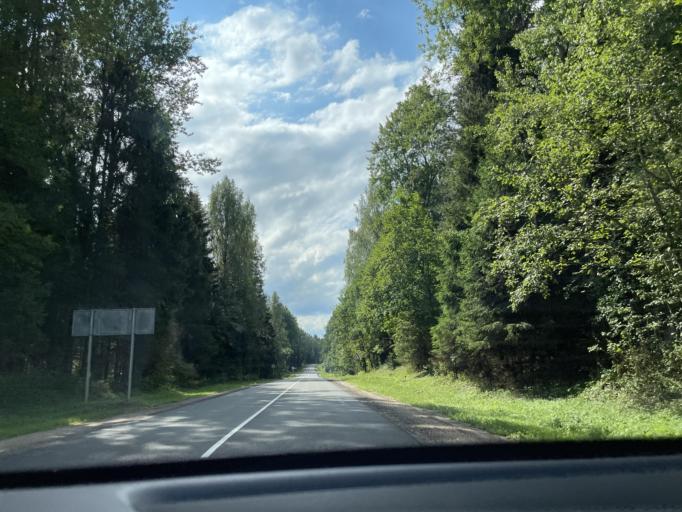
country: RU
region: Novgorod
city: Valday
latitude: 58.0342
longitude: 33.2188
